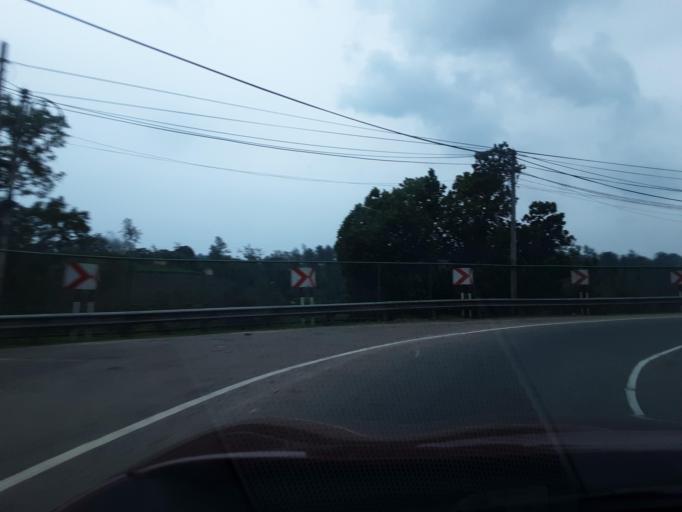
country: LK
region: Central
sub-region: Nuwara Eliya District
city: Nuwara Eliya
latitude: 6.9004
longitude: 80.9055
